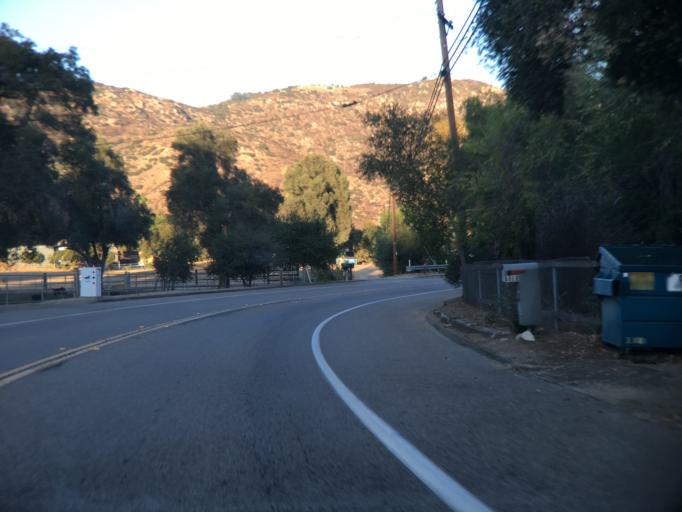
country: US
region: California
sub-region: San Diego County
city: Harbison Canyon
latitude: 32.8031
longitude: -116.8207
